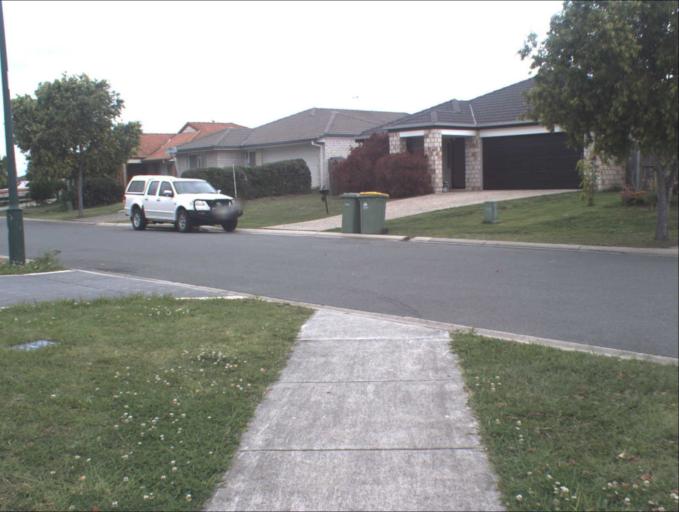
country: AU
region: Queensland
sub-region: Logan
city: Waterford West
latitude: -27.6949
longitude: 153.1140
